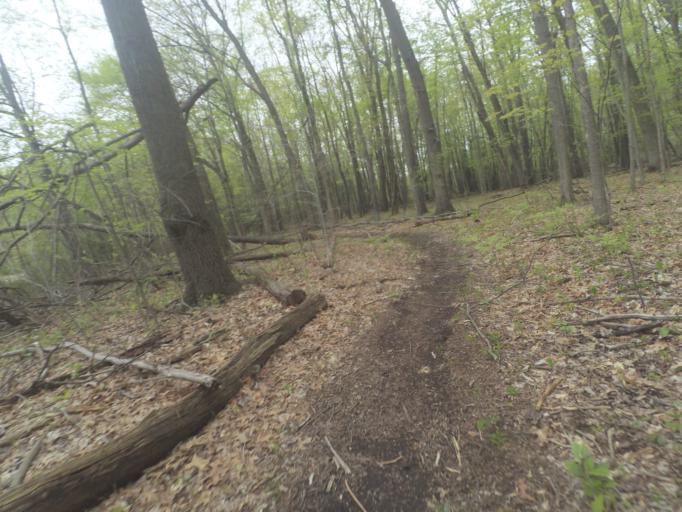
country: US
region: Ohio
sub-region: Portage County
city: Ravenna
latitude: 41.1726
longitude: -81.2986
